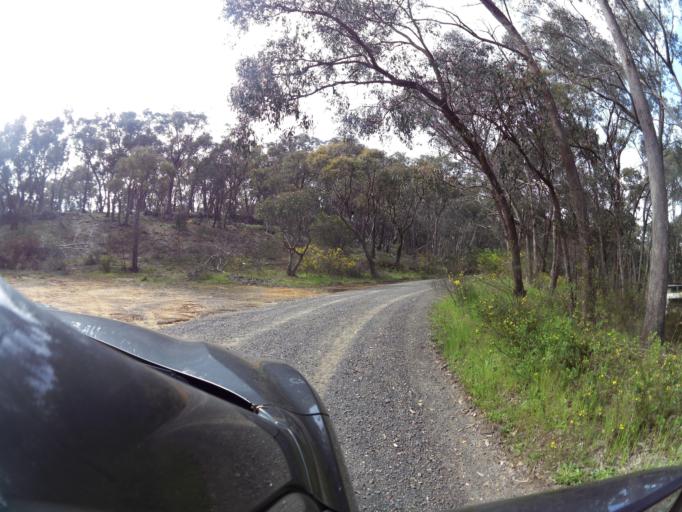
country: AU
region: Victoria
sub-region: Mount Alexander
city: Castlemaine
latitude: -37.3065
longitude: 144.1442
